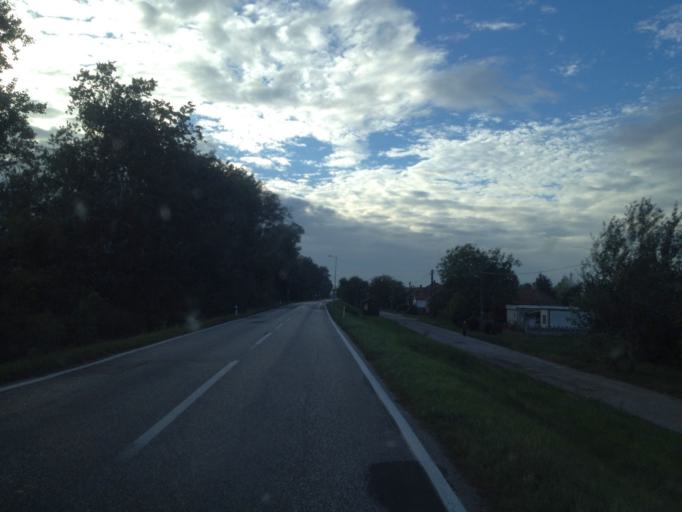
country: HU
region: Komarom-Esztergom
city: Almasfuzito
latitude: 47.7398
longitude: 18.2834
